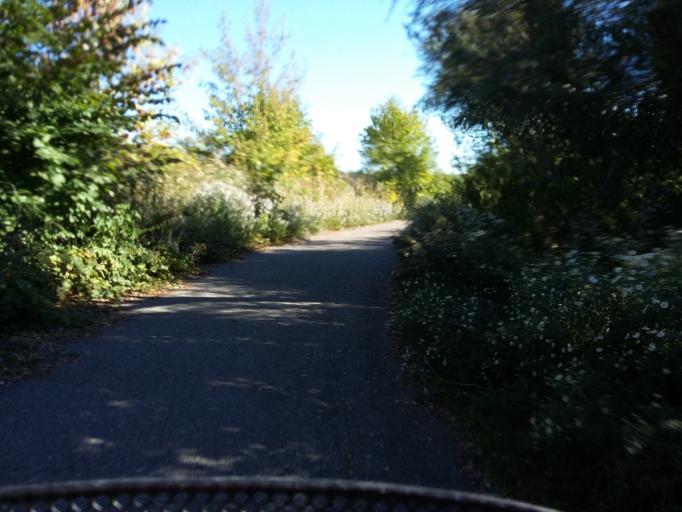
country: AT
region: Lower Austria
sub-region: Politischer Bezirk Ganserndorf
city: Marchegg
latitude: 48.2737
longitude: 16.9537
